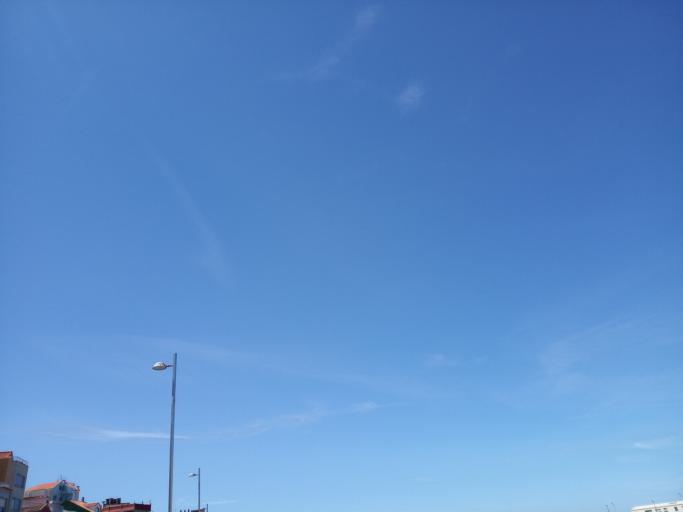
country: ES
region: Galicia
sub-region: Provincia de Pontevedra
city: A Guarda
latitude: 41.8993
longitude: -8.8741
